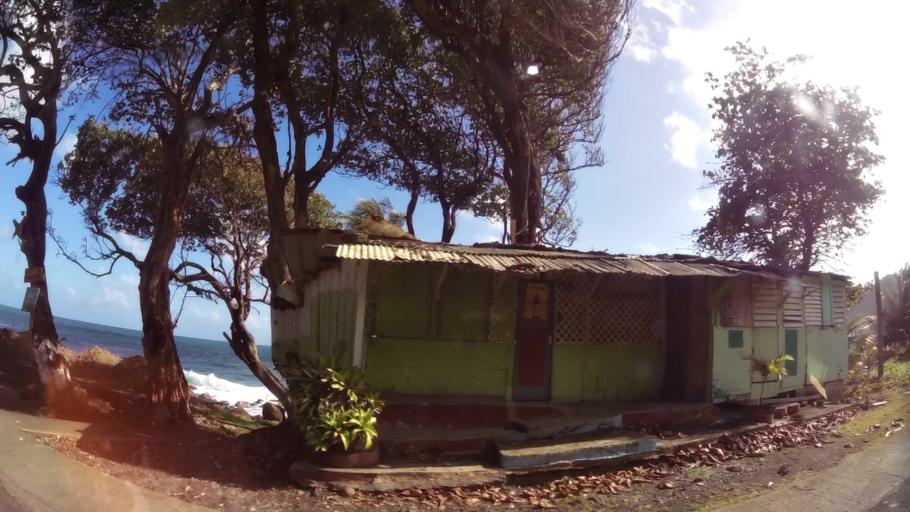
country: DM
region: Saint Andrew
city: Marigot
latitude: 15.5440
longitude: -61.2879
